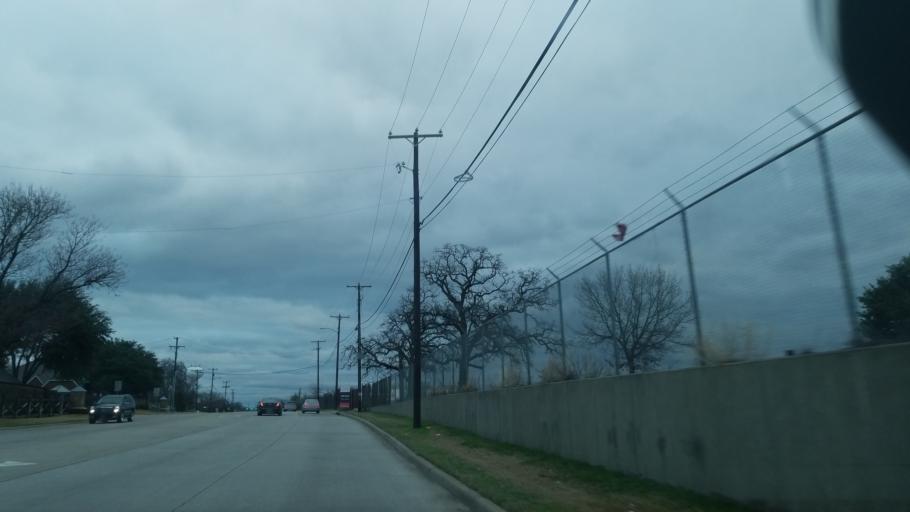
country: US
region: Texas
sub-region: Denton County
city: Hickory Creek
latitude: 33.1298
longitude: -97.0367
